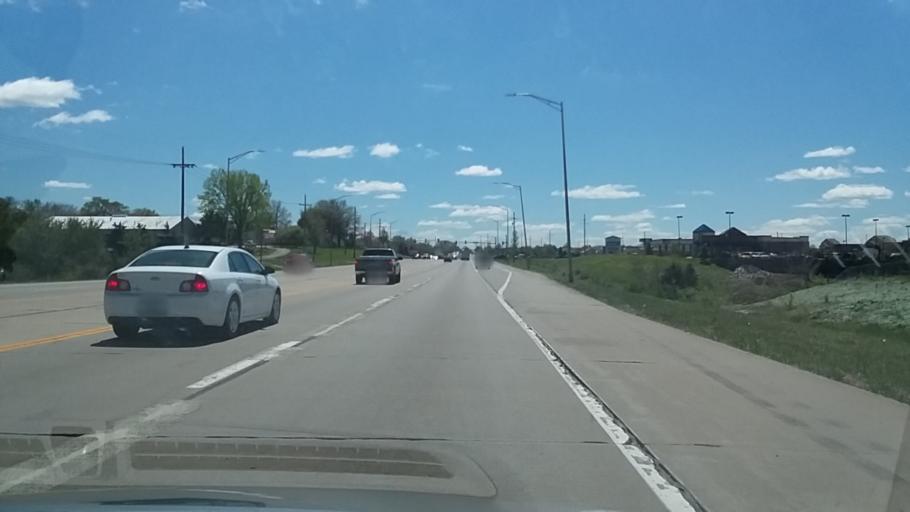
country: US
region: Kansas
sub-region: Johnson County
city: Olathe
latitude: 38.8899
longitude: -94.8349
